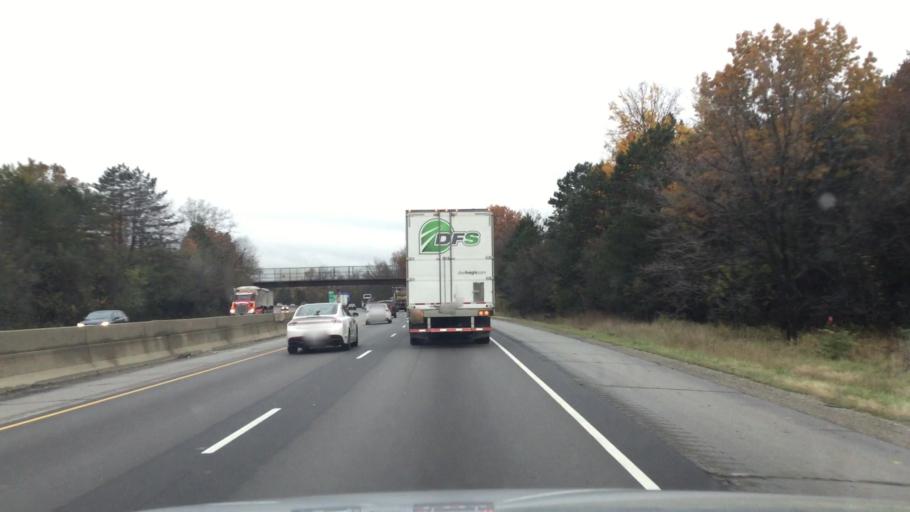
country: US
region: Michigan
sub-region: Washtenaw County
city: Ann Arbor
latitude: 42.2360
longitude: -83.7075
